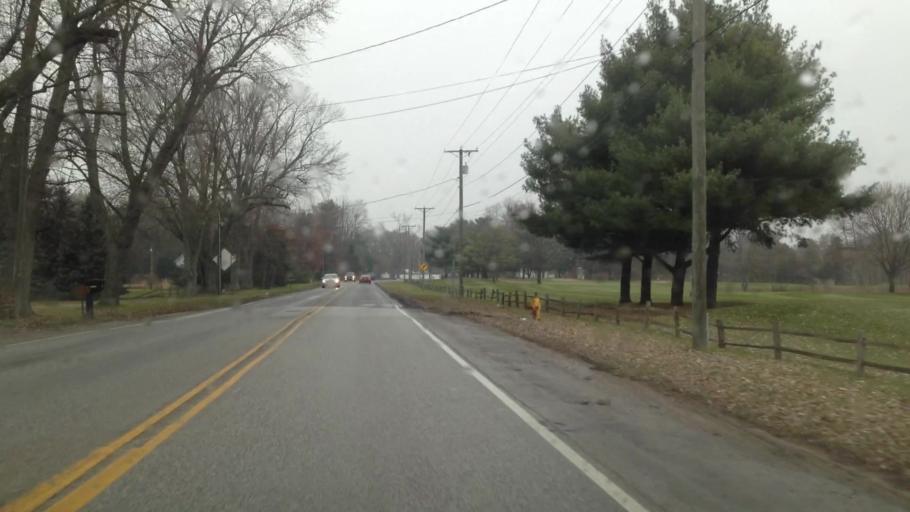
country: US
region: Indiana
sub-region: Saint Joseph County
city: Mishawaka
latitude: 41.7109
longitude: -86.1617
